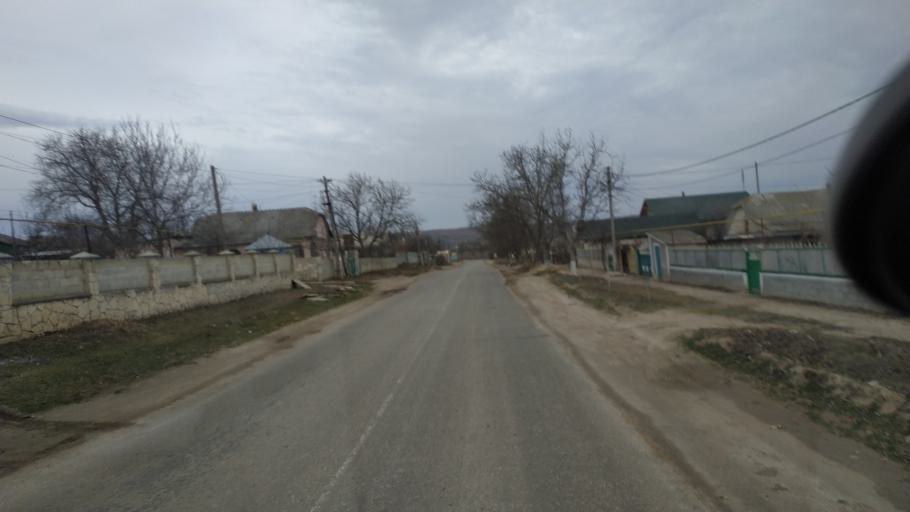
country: MD
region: Telenesti
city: Dubasari
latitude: 47.2462
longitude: 29.1399
